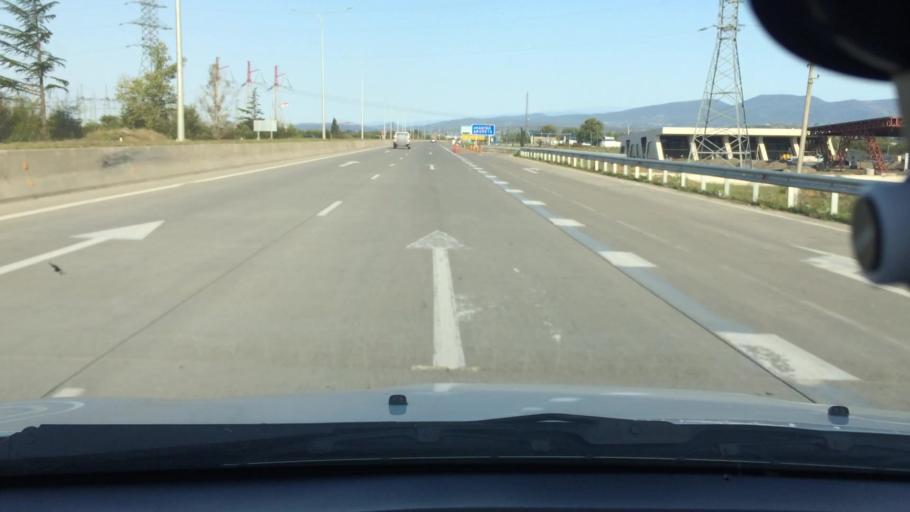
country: GE
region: Imereti
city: Zestap'oni
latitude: 42.1459
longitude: 42.9665
